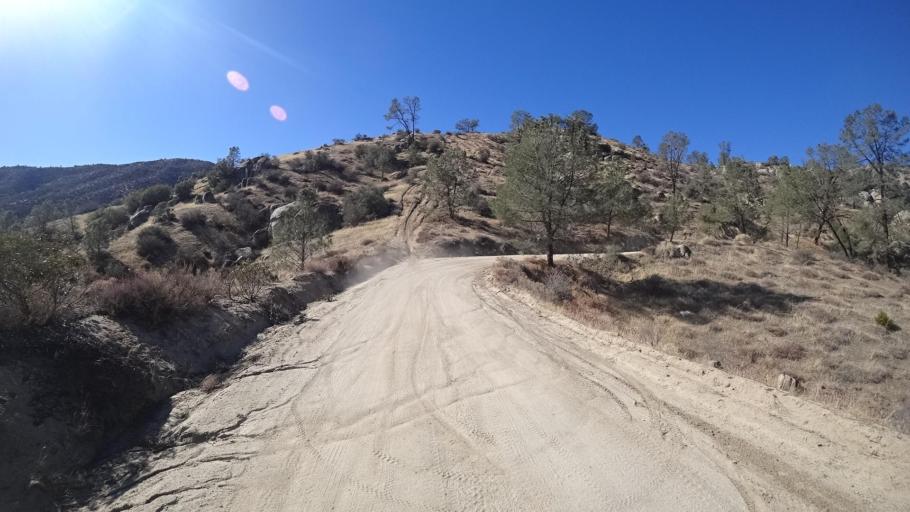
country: US
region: California
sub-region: Kern County
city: Wofford Heights
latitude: 35.7004
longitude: -118.4859
